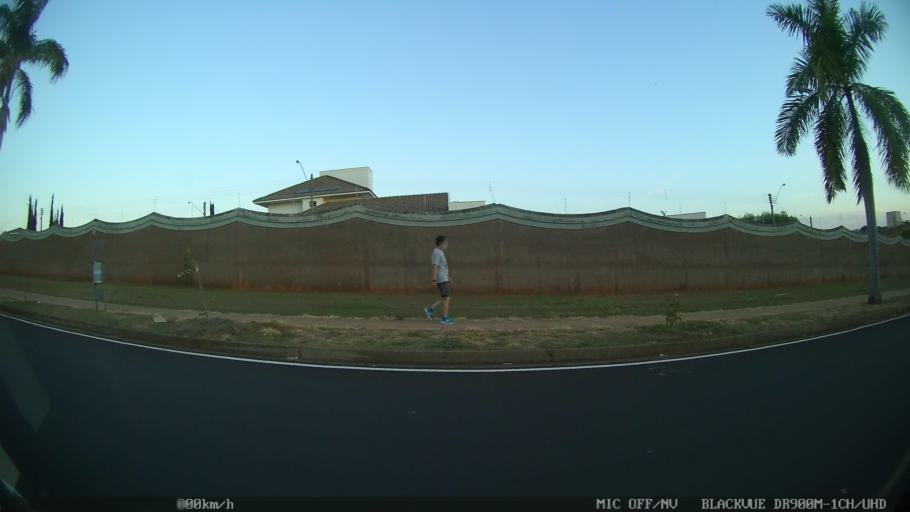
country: BR
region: Sao Paulo
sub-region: Sao Jose Do Rio Preto
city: Sao Jose do Rio Preto
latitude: -20.8166
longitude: -49.3458
